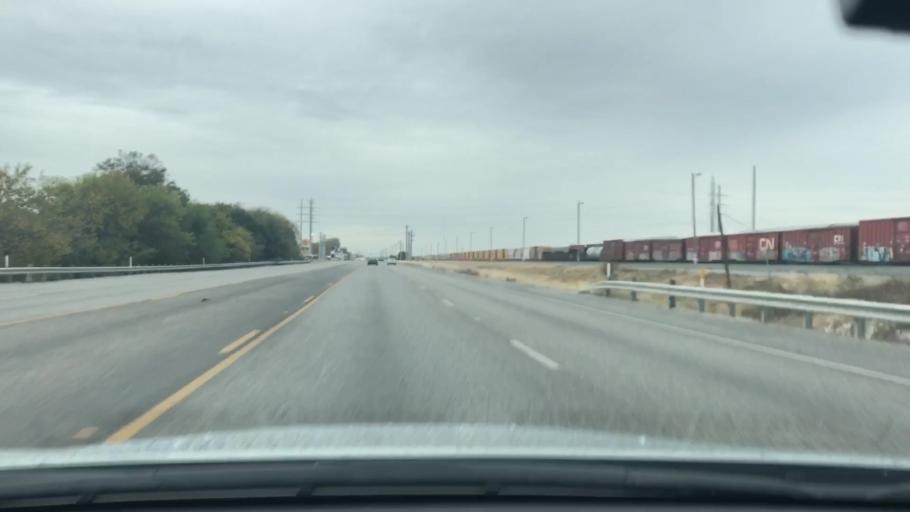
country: US
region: Texas
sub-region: Bexar County
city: Kirby
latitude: 29.4696
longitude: -98.3895
